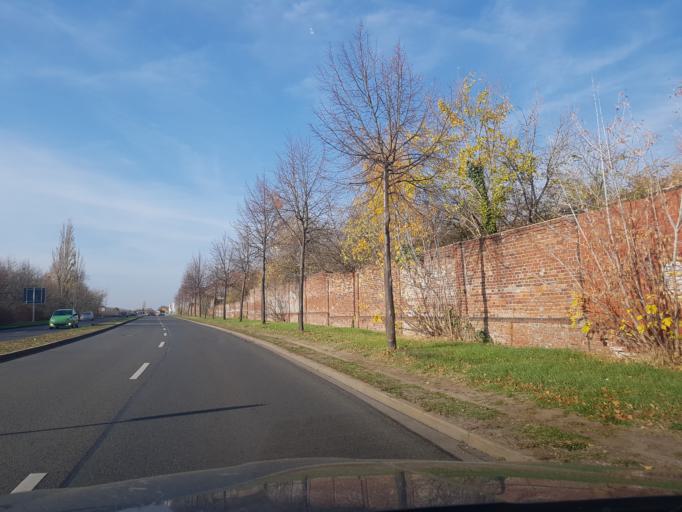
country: DE
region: Saxony
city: Torgau
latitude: 51.5603
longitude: 12.9808
